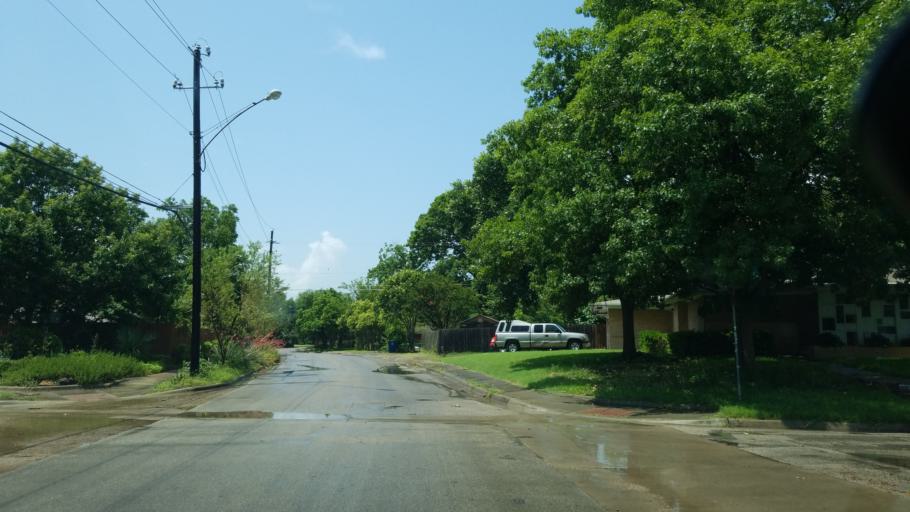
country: US
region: Texas
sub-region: Dallas County
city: Farmers Branch
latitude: 32.8781
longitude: -96.8710
